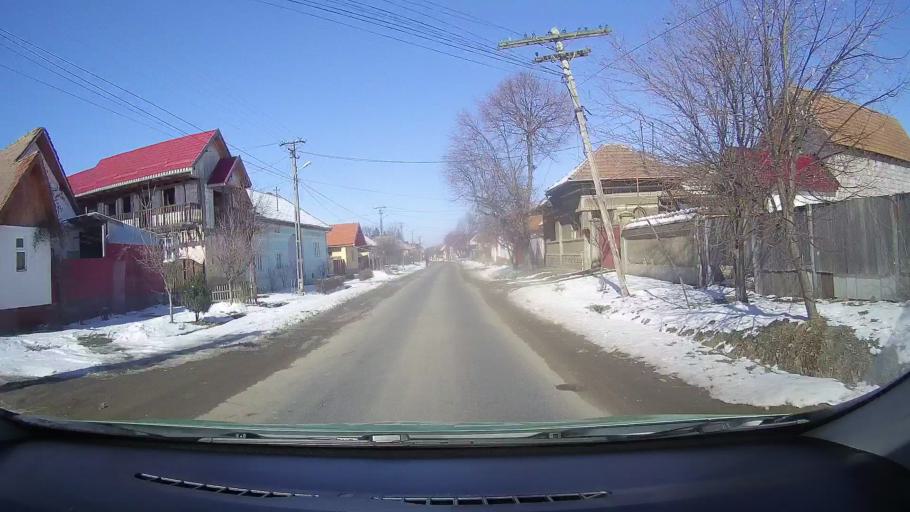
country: RO
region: Brasov
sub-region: Comuna Harseni
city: Harseni
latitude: 45.7509
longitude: 25.0141
